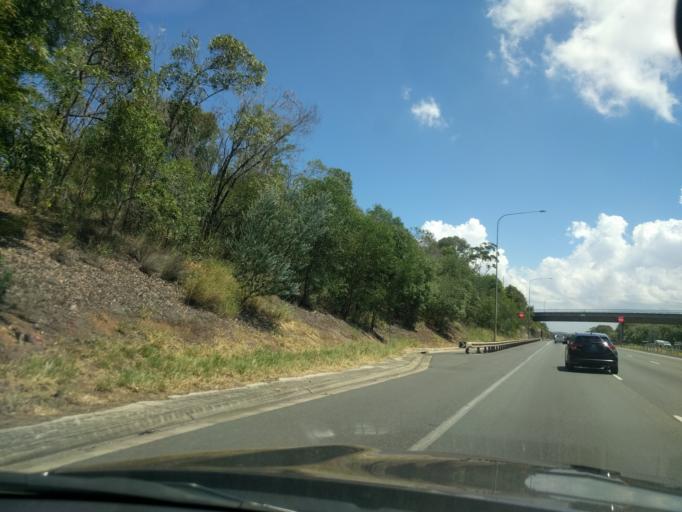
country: AU
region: Queensland
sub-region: Moreton Bay
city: Murrumba Downs
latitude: -27.2582
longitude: 153.0189
